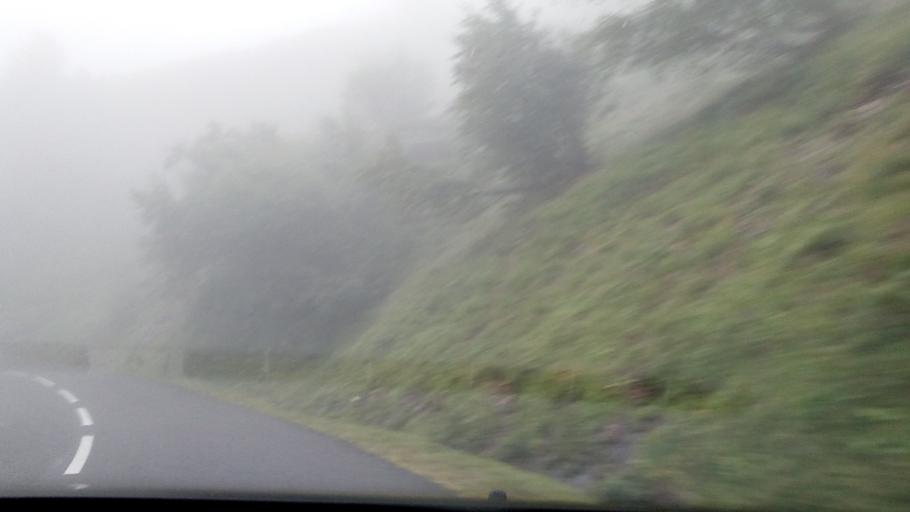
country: FR
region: Aquitaine
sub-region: Departement des Pyrenees-Atlantiques
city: Laruns
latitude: 42.9714
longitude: -0.3228
